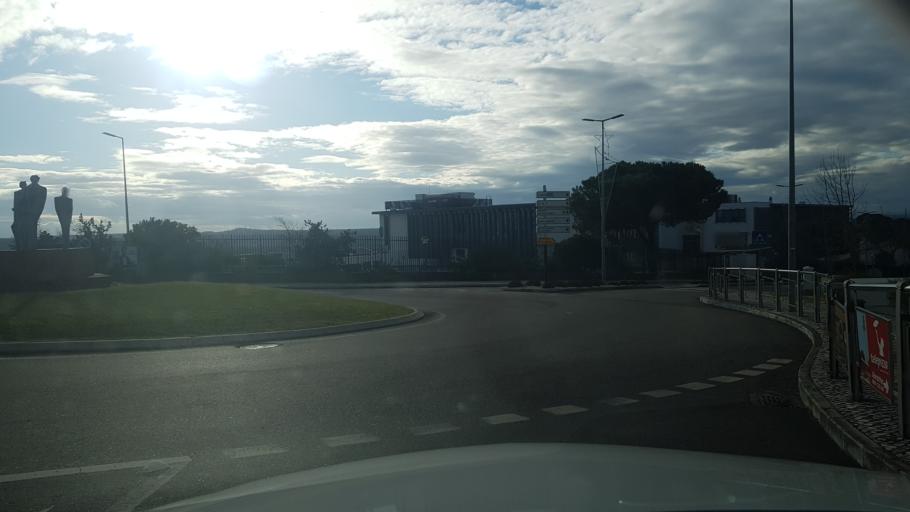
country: PT
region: Santarem
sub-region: Abrantes
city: Abrantes
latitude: 39.4629
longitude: -8.2058
